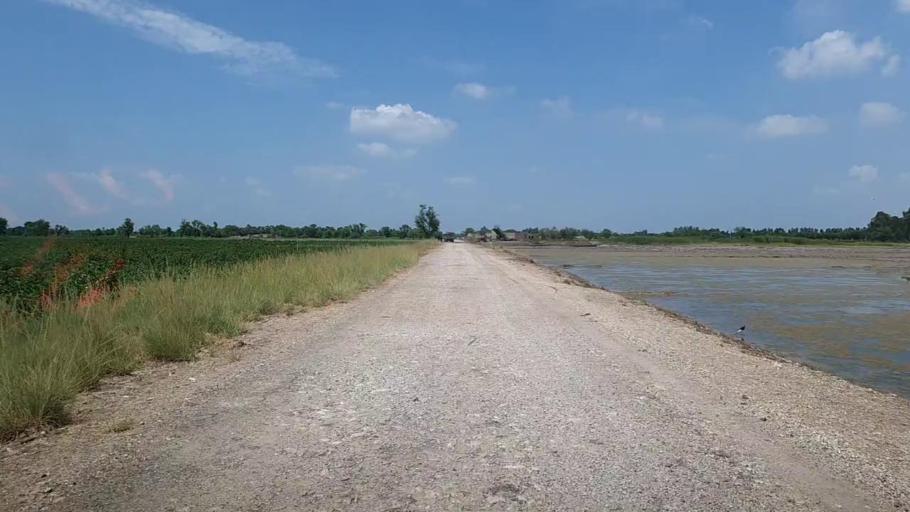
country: PK
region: Sindh
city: Bhiria
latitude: 26.9713
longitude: 68.2393
